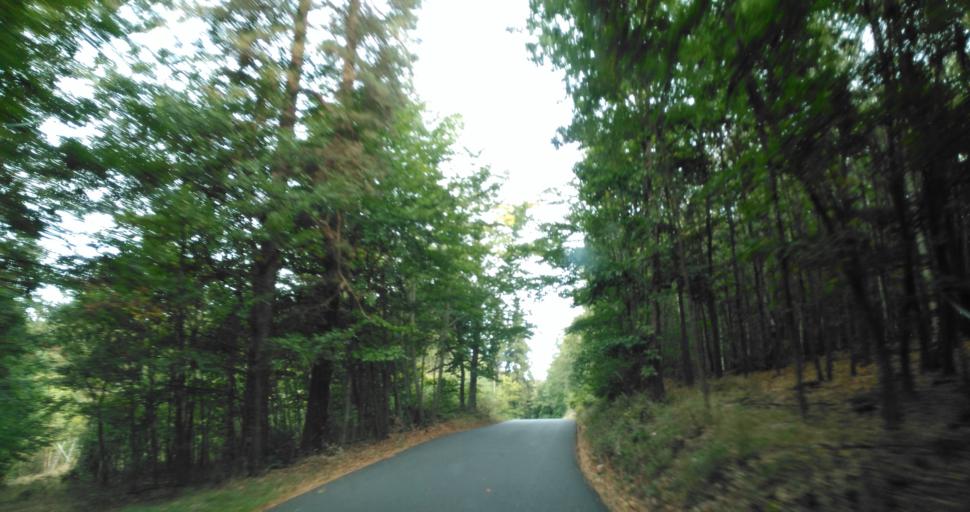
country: CZ
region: Plzensky
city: Zbiroh
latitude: 49.9341
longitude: 13.7781
